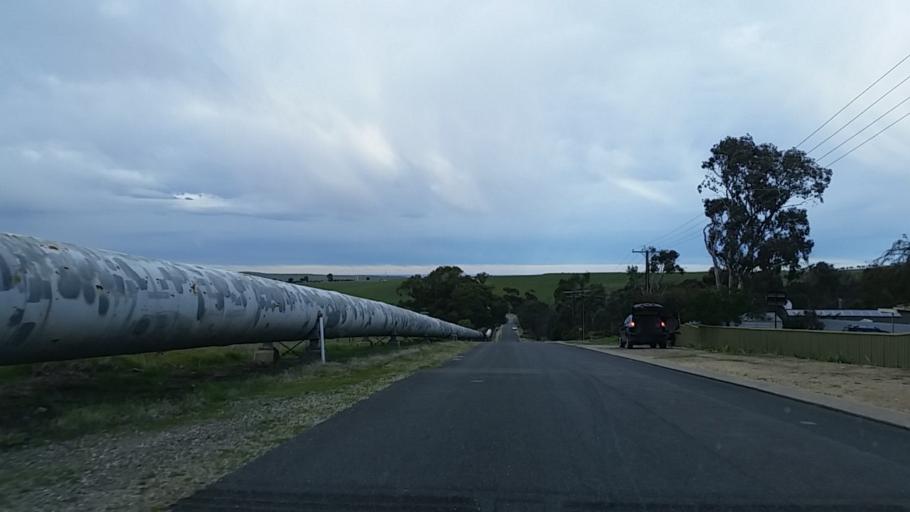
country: AU
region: South Australia
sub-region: Adelaide Hills
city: Birdwood
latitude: -34.8212
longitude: 139.0681
